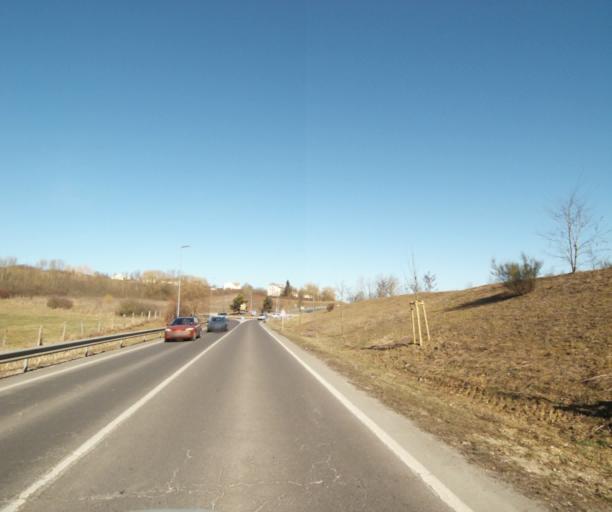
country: FR
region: Lorraine
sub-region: Departement de Meurthe-et-Moselle
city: Vandoeuvre-les-Nancy
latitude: 48.6333
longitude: 6.1809
